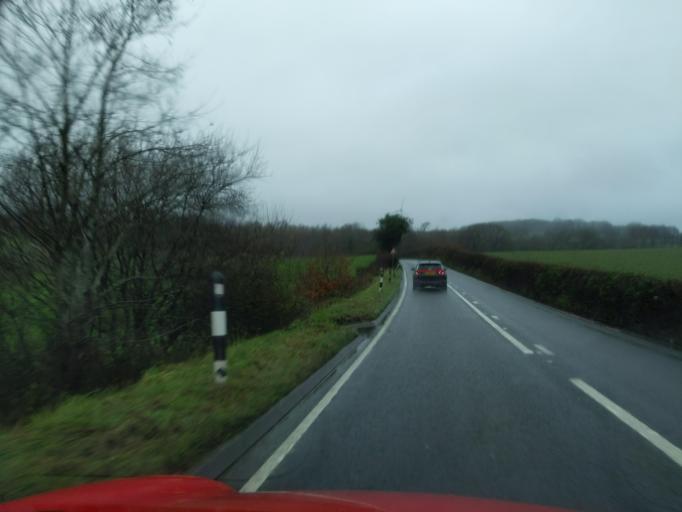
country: GB
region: England
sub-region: Cornwall
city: Launceston
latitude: 50.6113
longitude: -4.3367
